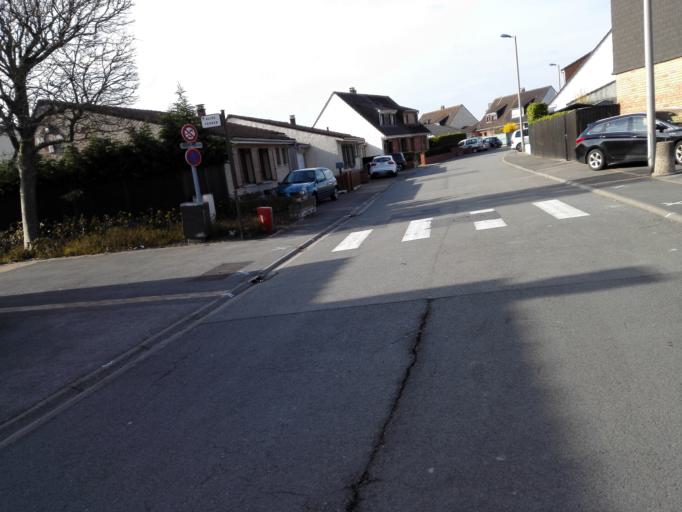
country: FR
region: Nord-Pas-de-Calais
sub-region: Departement du Nord
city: Grande-Synthe
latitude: 51.0027
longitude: 2.2934
